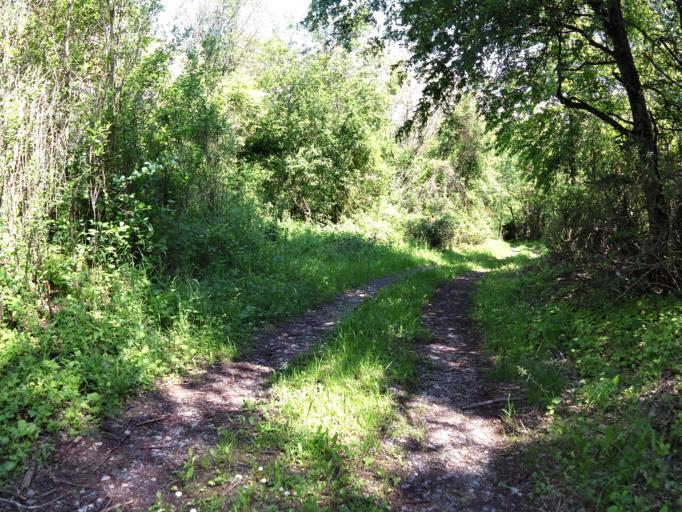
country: DE
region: Bavaria
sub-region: Regierungsbezirk Unterfranken
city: Eibelstadt
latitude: 49.7304
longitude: 10.0139
